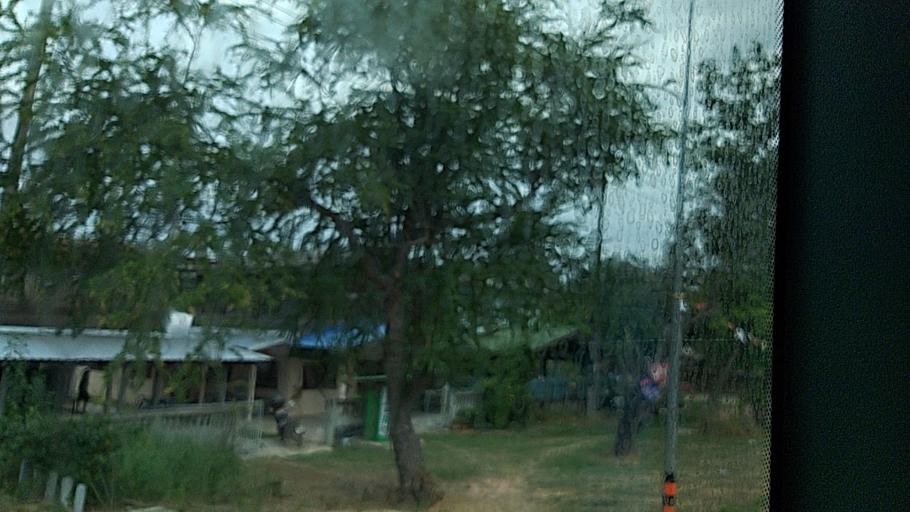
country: TH
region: Maha Sarakham
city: Maha Sarakham
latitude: 16.1487
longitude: 103.3978
